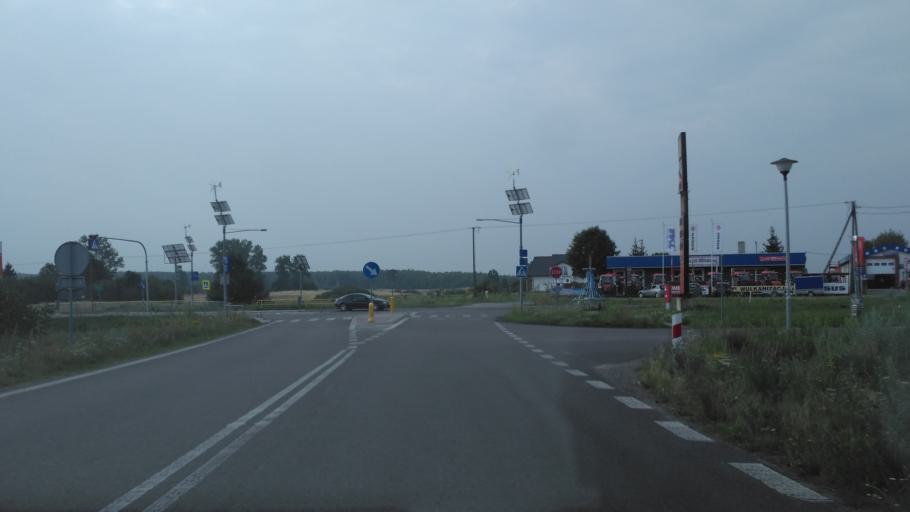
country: PL
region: Lublin Voivodeship
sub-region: Powiat chelmski
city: Rejowiec Fabryczny
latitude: 51.1766
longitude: 23.1777
